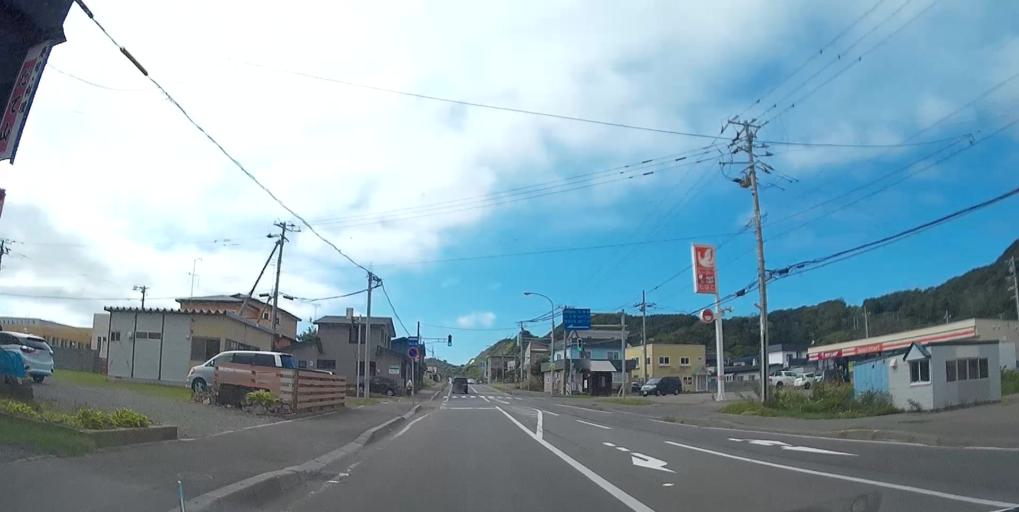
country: JP
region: Hokkaido
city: Kamiiso
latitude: 41.9741
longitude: 140.1391
